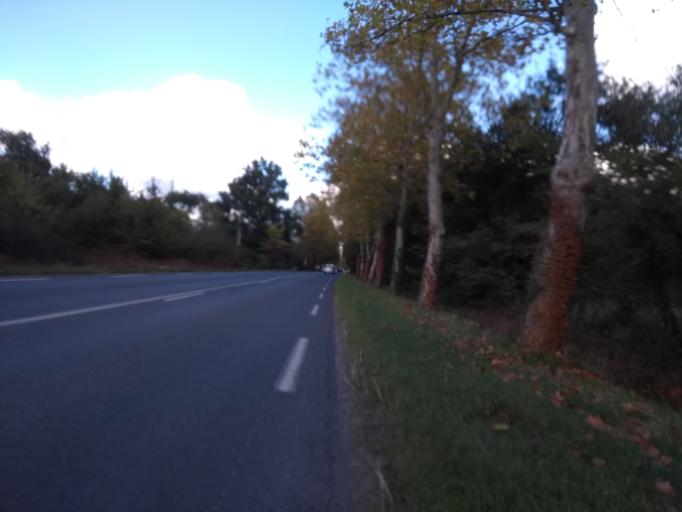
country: FR
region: Aquitaine
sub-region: Departement de la Gironde
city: Saint-Aubin-de-Medoc
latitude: 44.6820
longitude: -0.7240
